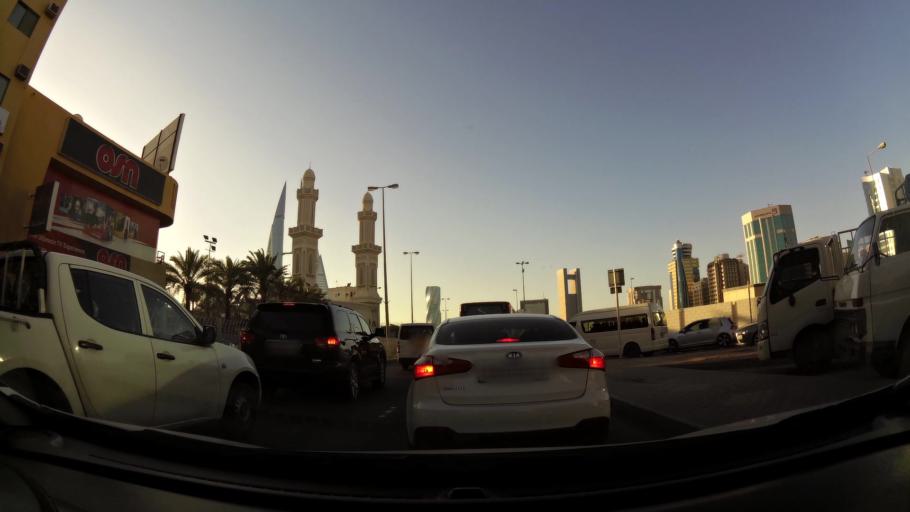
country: BH
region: Manama
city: Manama
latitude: 26.2366
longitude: 50.5871
